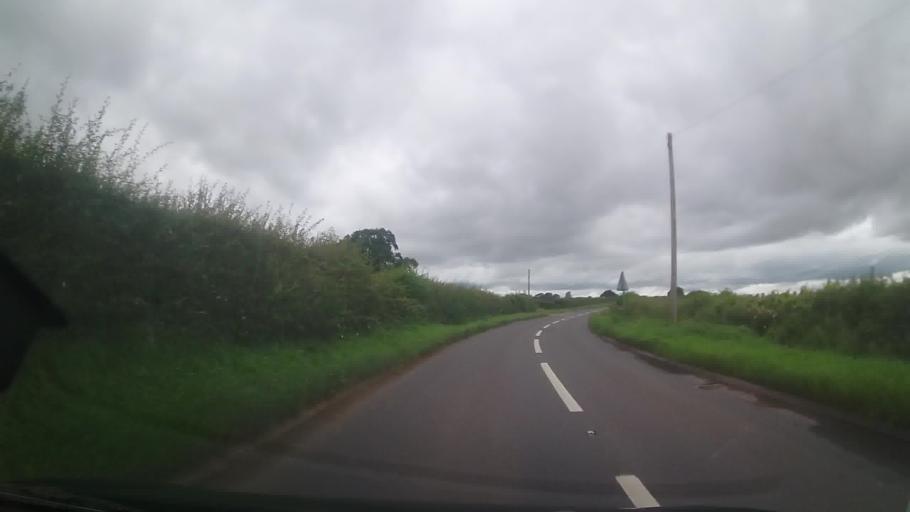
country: GB
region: England
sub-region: Shropshire
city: Petton
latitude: 52.8601
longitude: -2.8475
